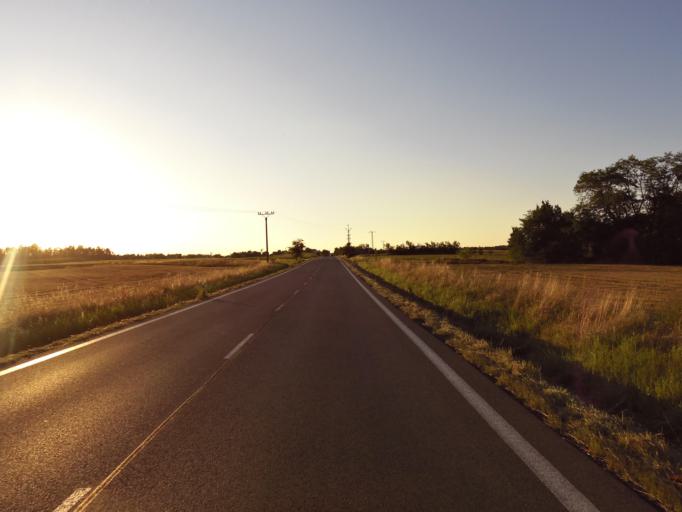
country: CZ
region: Central Bohemia
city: Mnichovo Hradiste
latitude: 50.5264
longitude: 14.9351
